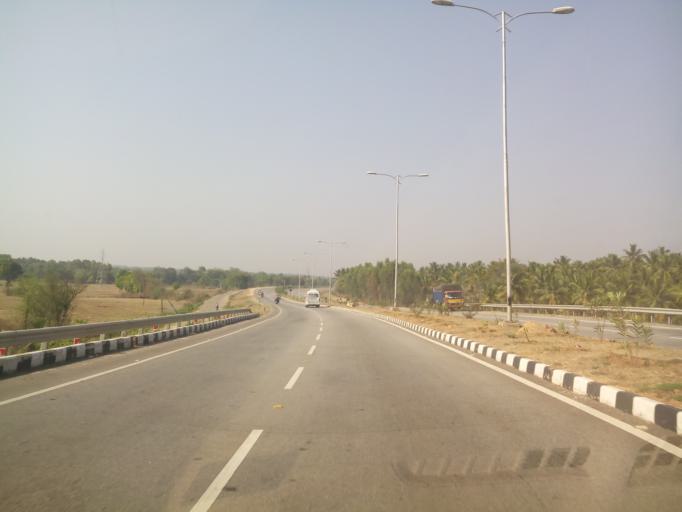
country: IN
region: Karnataka
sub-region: Tumkur
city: Kunigal
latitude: 13.0275
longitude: 77.0758
